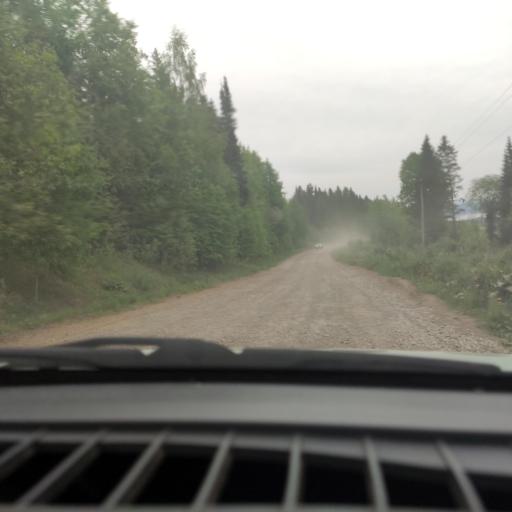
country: RU
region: Perm
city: Novyye Lyady
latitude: 57.9167
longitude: 56.6598
